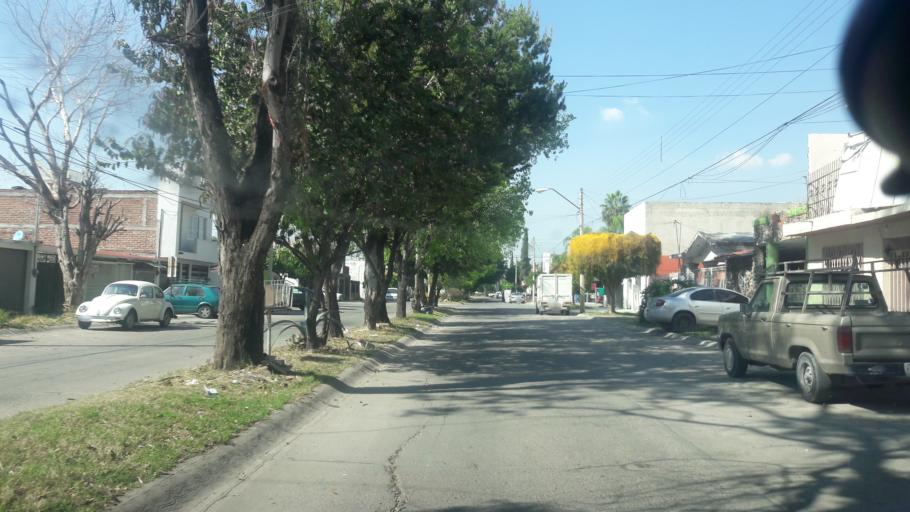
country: MX
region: Guanajuato
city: Leon
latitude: 21.1803
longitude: -101.6648
